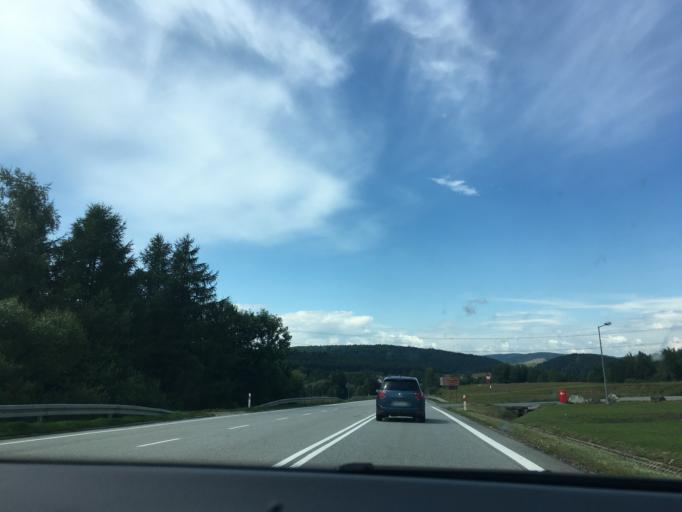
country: PL
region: Subcarpathian Voivodeship
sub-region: Powiat krosnienski
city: Jasliska
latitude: 49.4249
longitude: 21.6922
